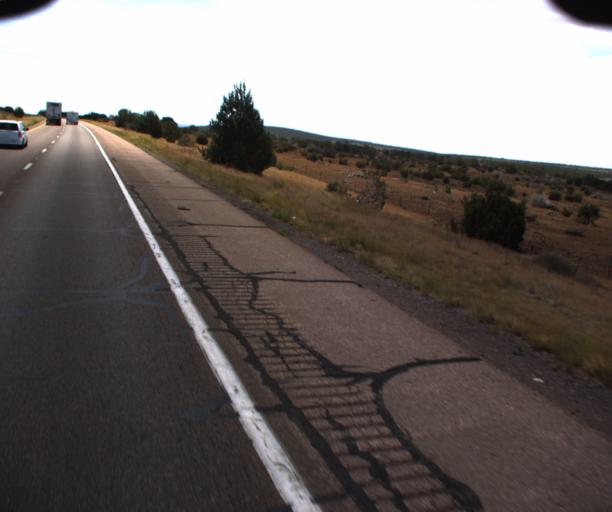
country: US
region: Arizona
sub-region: Yavapai County
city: Paulden
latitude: 35.2654
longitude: -112.7245
